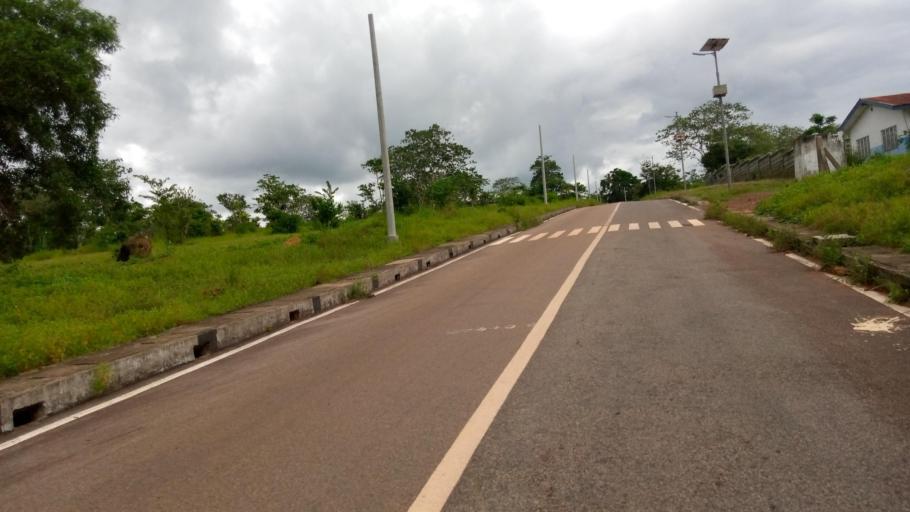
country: SL
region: Southern Province
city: Moyamba
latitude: 8.1614
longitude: -12.4411
